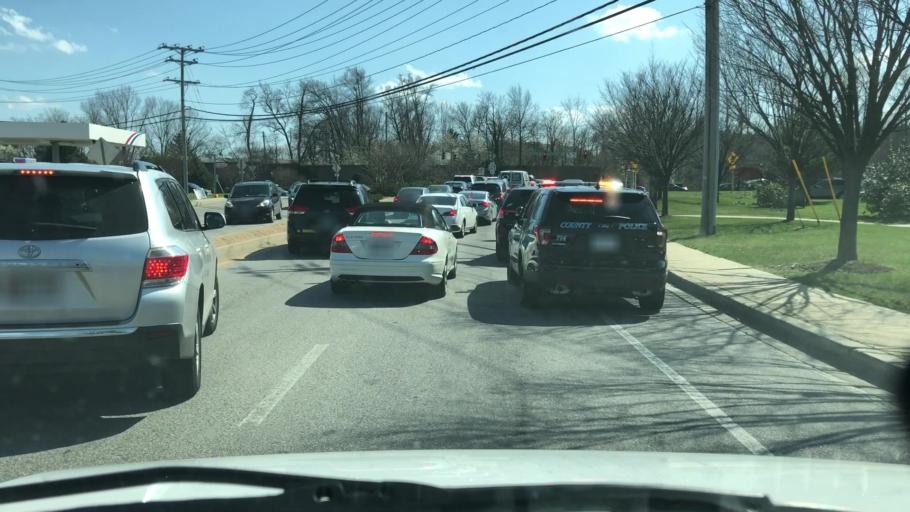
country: US
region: Maryland
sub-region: Anne Arundel County
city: Parole
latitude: 38.9737
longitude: -76.5248
